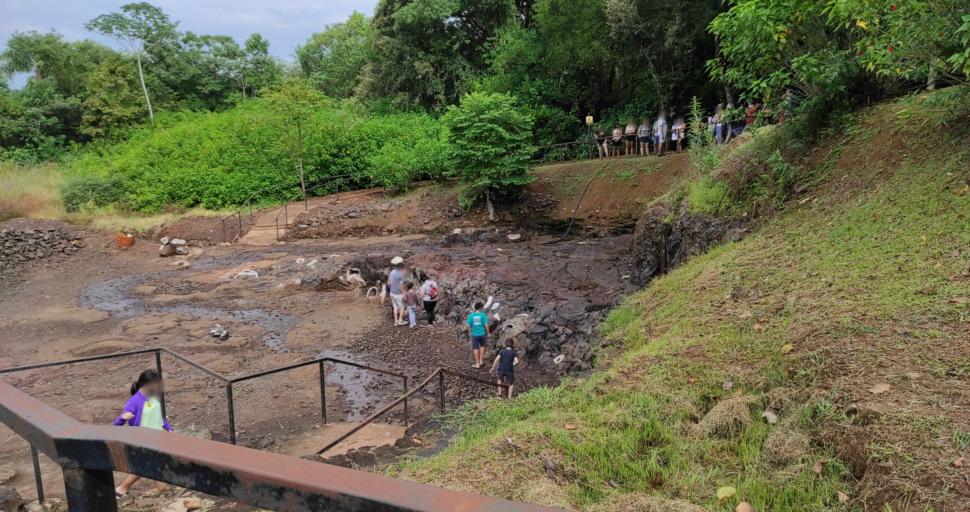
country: AR
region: Misiones
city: Puerto Libertad
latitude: -25.9577
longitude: -54.5993
